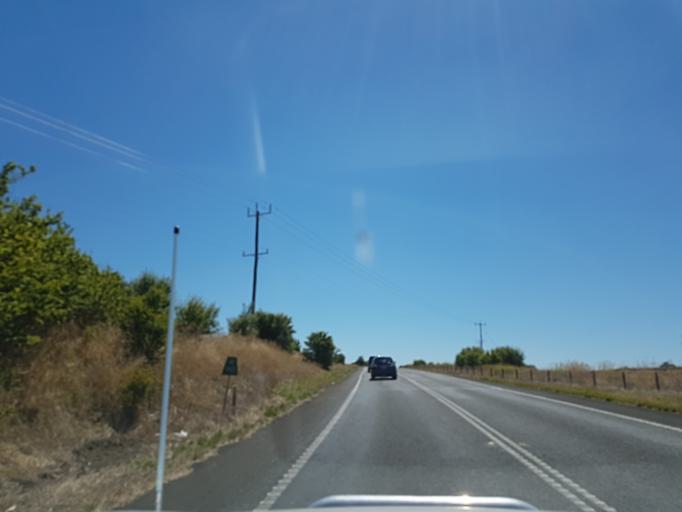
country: AU
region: Victoria
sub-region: Colac-Otway
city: Colac
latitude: -38.3222
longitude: 143.3366
